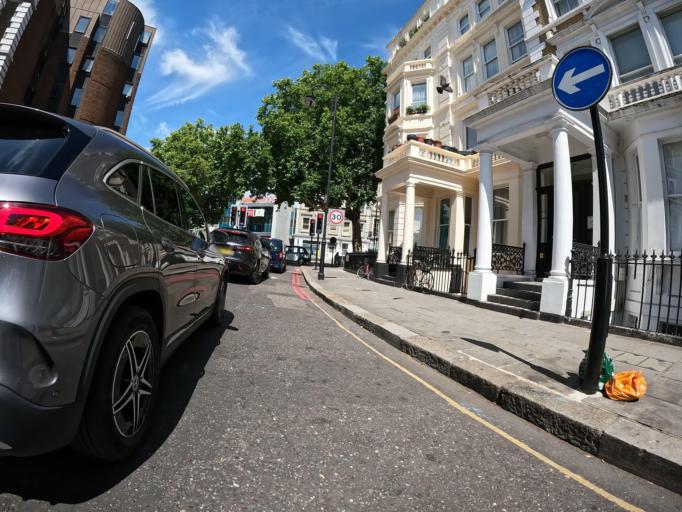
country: GB
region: England
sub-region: Greater London
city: Kensington
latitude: 51.4942
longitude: -0.1887
